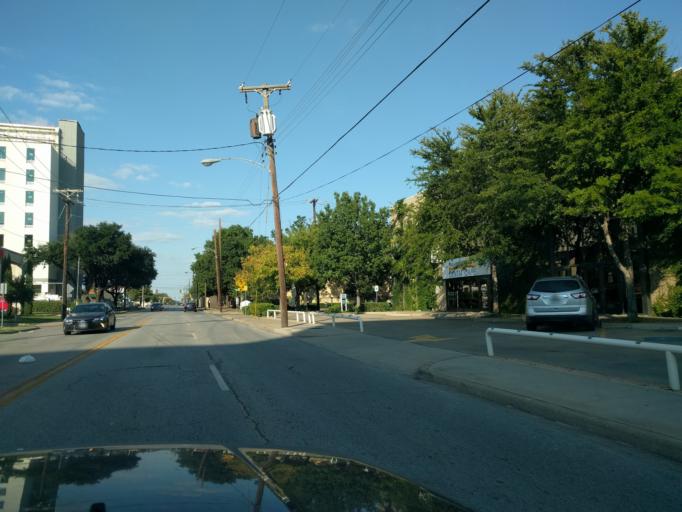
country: US
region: Texas
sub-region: Dallas County
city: Dallas
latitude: 32.7926
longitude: -96.7784
